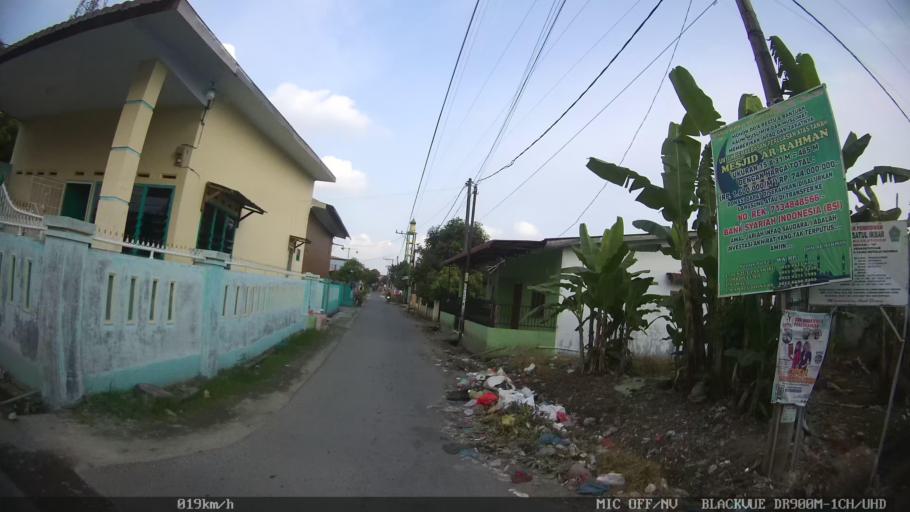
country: ID
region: North Sumatra
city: Medan
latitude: 3.5947
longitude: 98.7437
